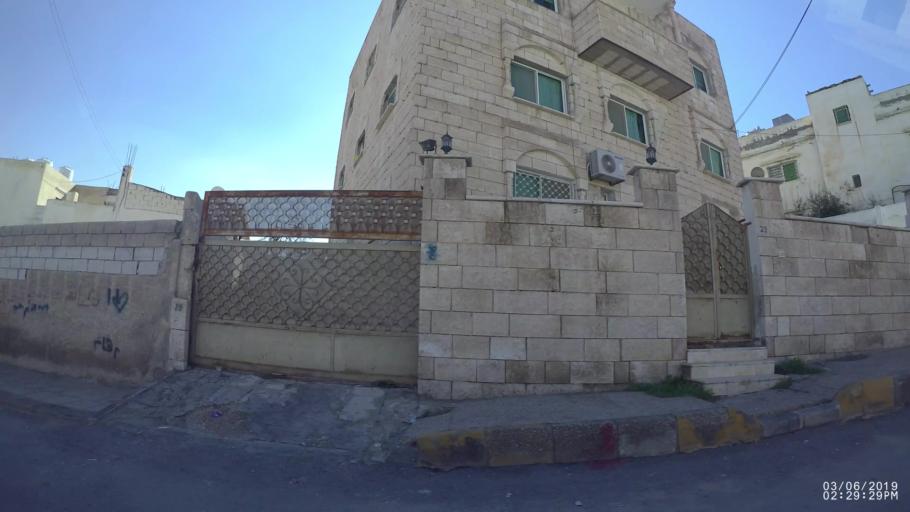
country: JO
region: Zarqa
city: Russeifa
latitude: 32.0337
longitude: 36.0372
